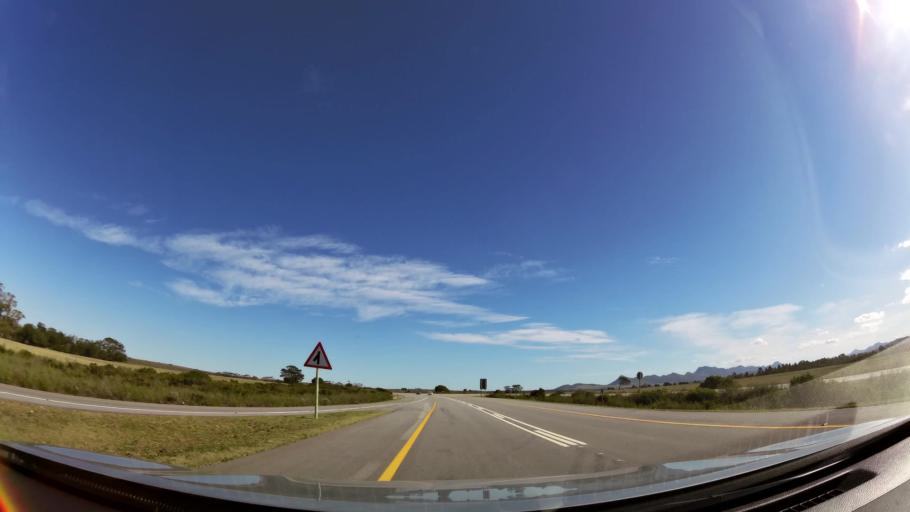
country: ZA
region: Eastern Cape
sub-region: Cacadu District Municipality
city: Kruisfontein
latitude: -34.0302
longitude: 24.5983
